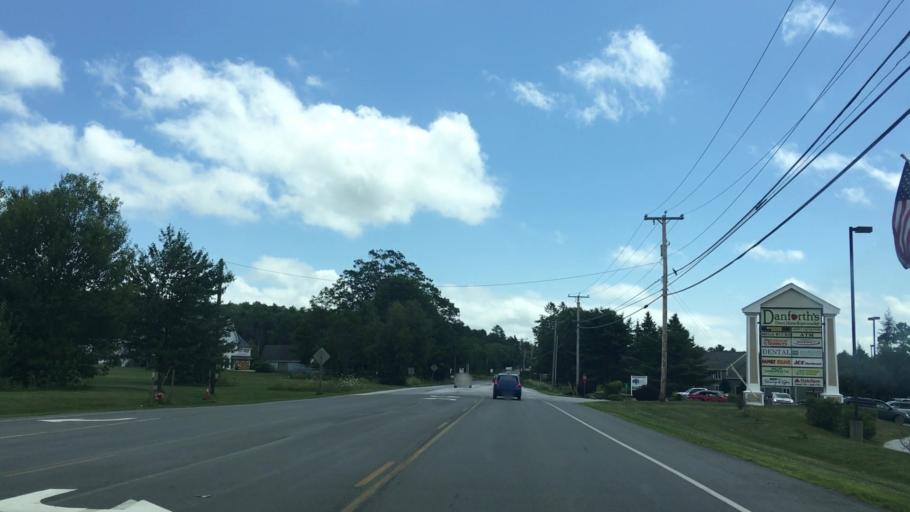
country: US
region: Maine
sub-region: Penobscot County
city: Hermon
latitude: 44.8060
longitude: -68.9026
